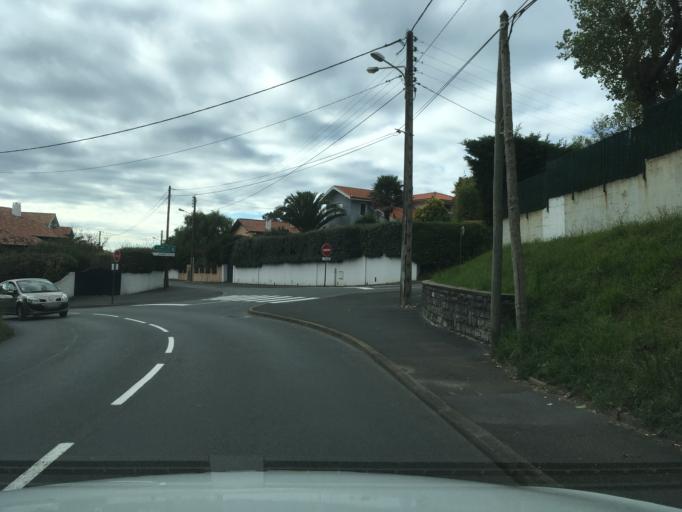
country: FR
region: Aquitaine
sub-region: Departement des Pyrenees-Atlantiques
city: Biarritz
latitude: 43.4623
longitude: -1.5682
